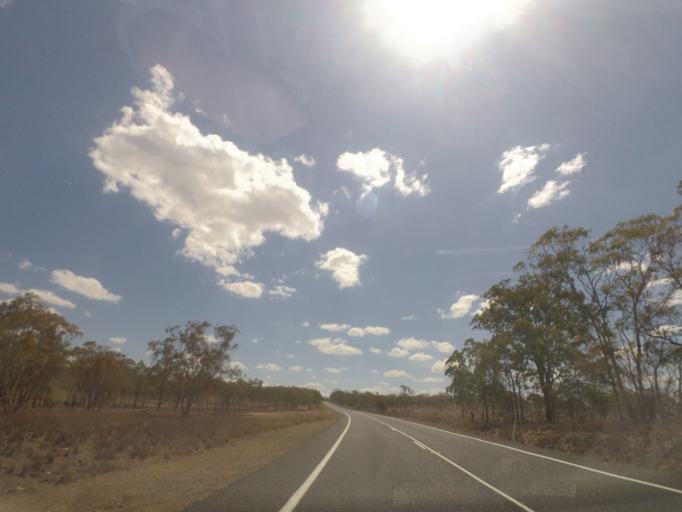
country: AU
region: Queensland
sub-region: Southern Downs
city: Warwick
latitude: -28.1610
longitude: 151.6896
